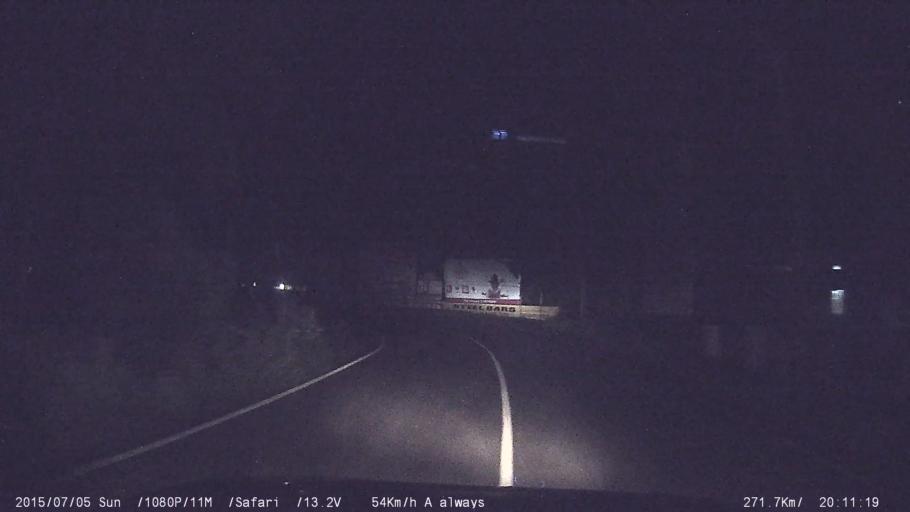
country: IN
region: Kerala
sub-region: Palakkad district
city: Palakkad
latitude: 10.8563
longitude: 76.5717
